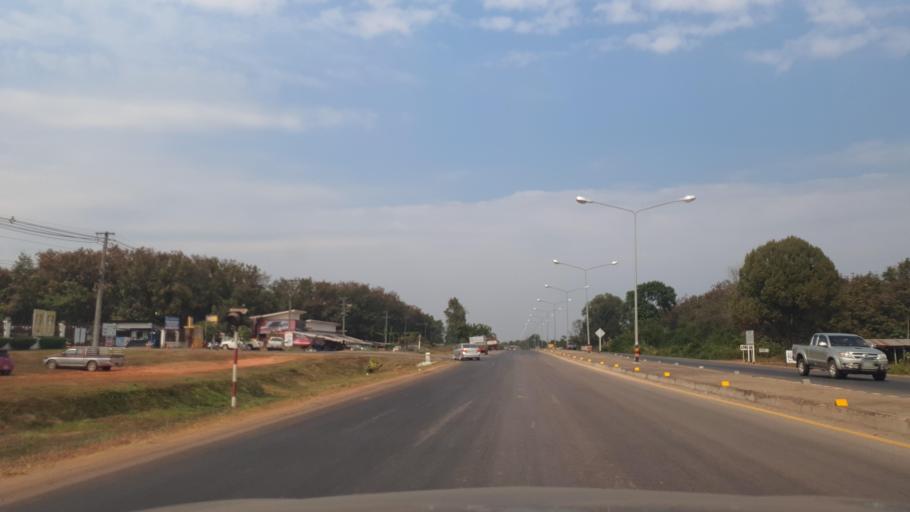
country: TH
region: Changwat Bueng Kan
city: Si Wilai
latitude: 18.2986
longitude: 103.8174
